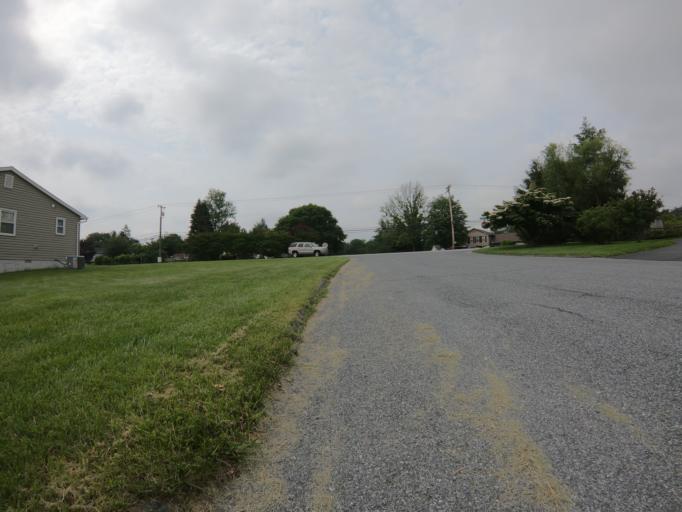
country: US
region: Maryland
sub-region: Howard County
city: Columbia
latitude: 39.2564
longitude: -76.8594
